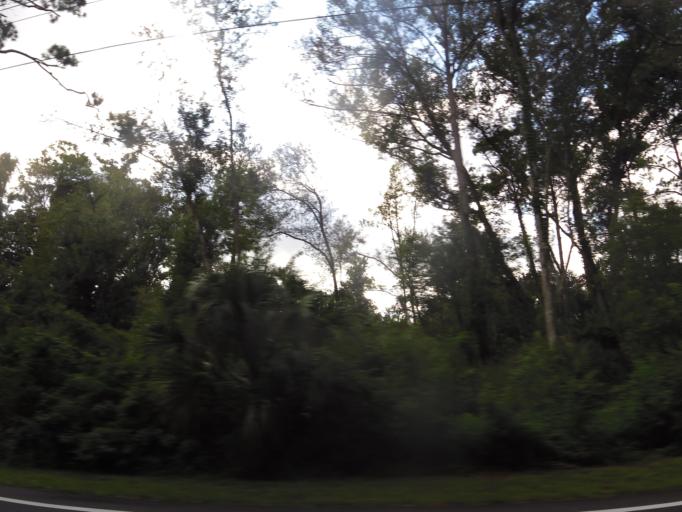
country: US
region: Georgia
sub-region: Glynn County
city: Saint Simons Island
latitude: 31.1686
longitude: -81.3835
